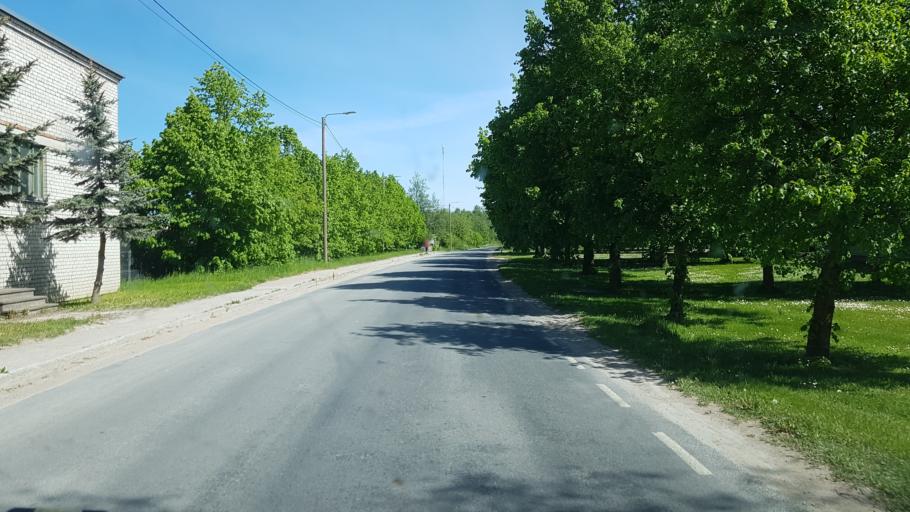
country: EE
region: Saare
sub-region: Kuressaare linn
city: Kuressaare
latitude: 58.2695
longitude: 22.4915
